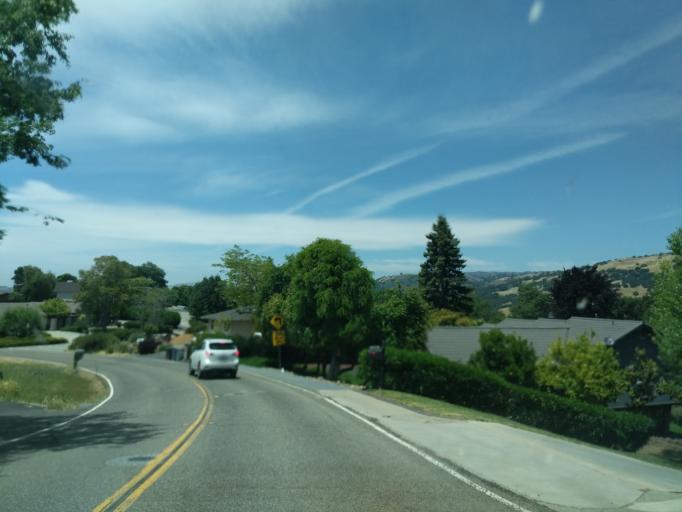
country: US
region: California
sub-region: Santa Clara County
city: San Martin
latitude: 37.1409
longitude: -121.5894
